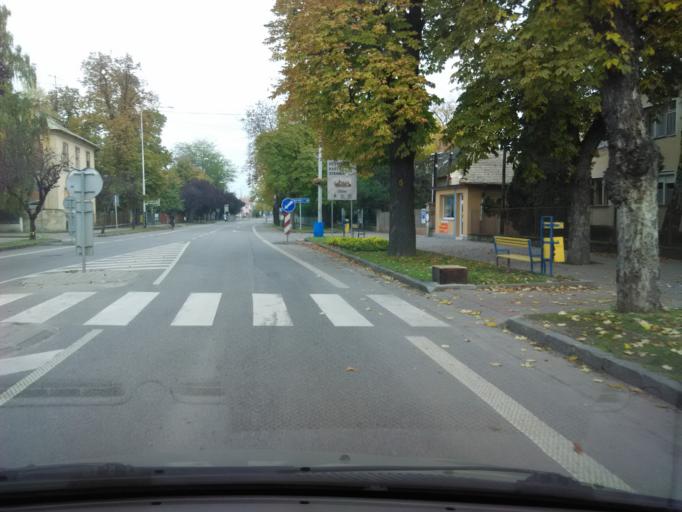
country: SK
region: Nitriansky
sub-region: Okres Komarno
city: Hurbanovo
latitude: 47.8717
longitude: 18.1909
